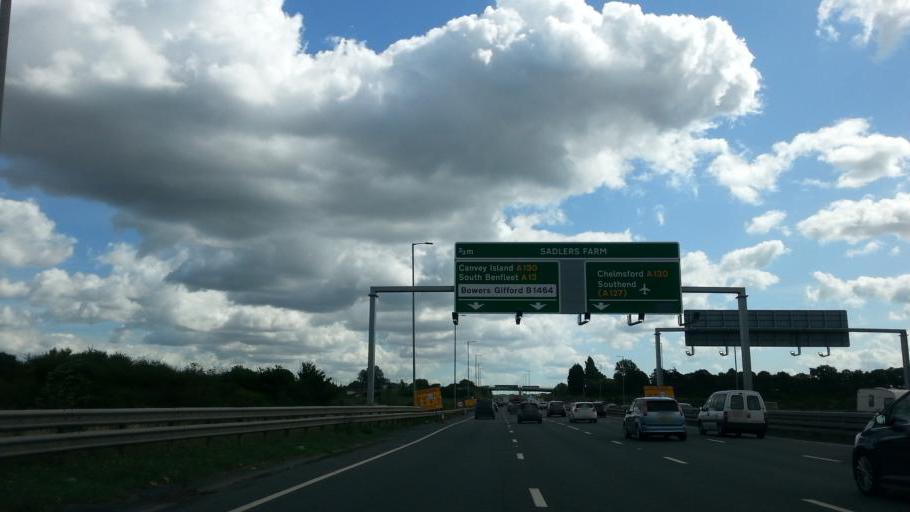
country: GB
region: England
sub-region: Essex
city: Pitsea
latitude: 51.5650
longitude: 0.5156
